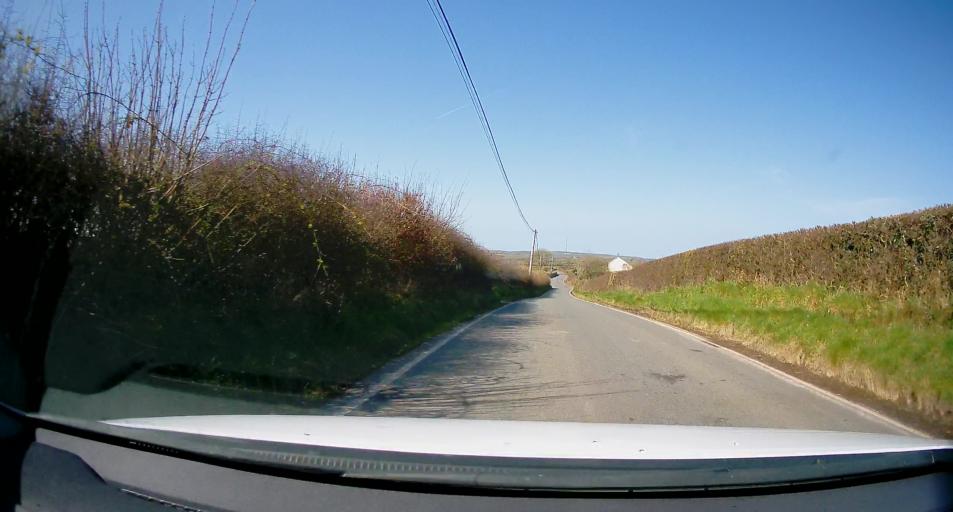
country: GB
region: Wales
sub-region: County of Ceredigion
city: Penparcau
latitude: 52.3226
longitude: -4.0668
